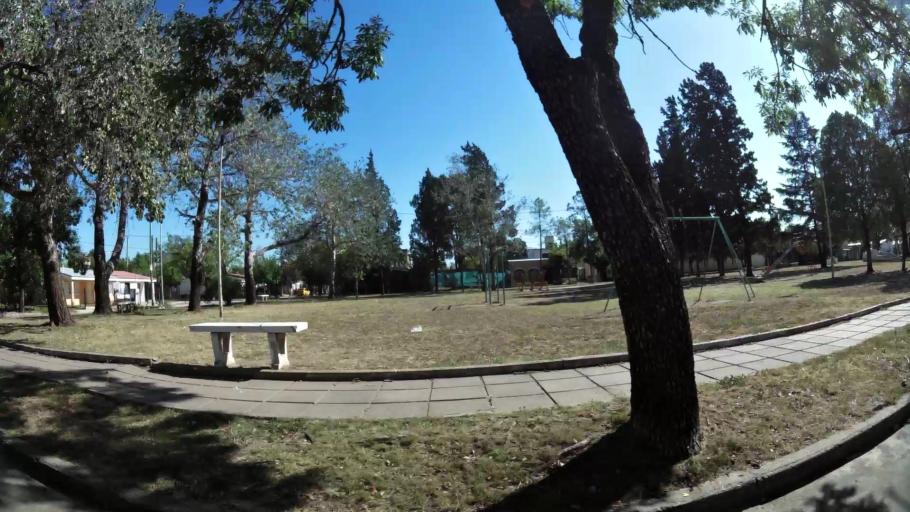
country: AR
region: Cordoba
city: Villa Allende
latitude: -31.3418
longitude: -64.2398
